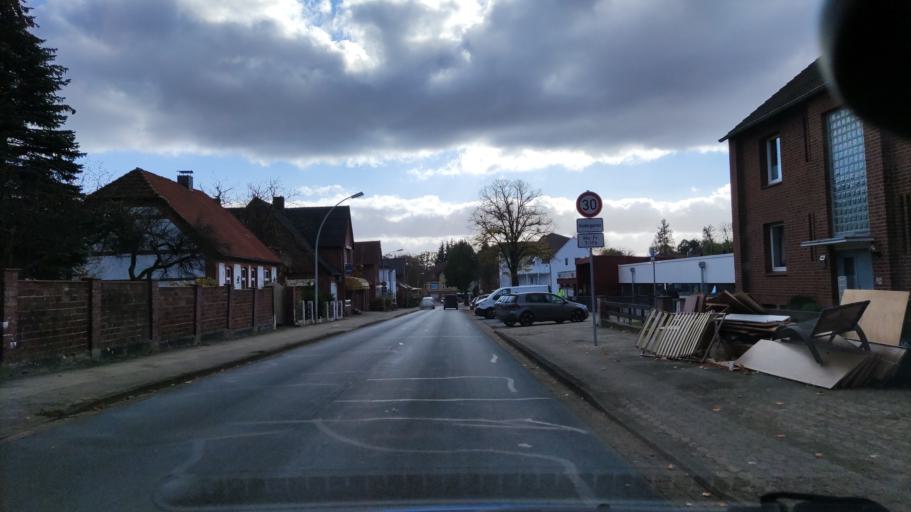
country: DE
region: Lower Saxony
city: Munster
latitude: 52.9883
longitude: 10.0924
